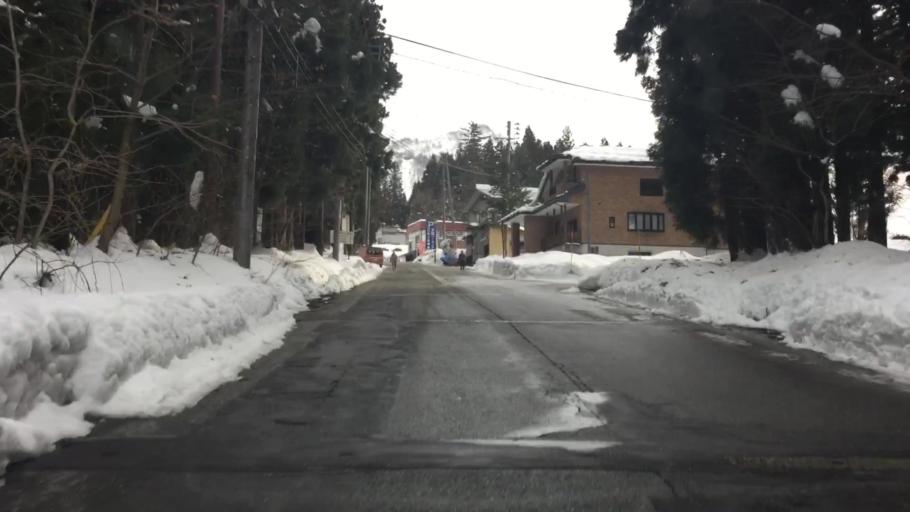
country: JP
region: Niigata
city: Shiozawa
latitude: 36.9885
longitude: 138.8217
